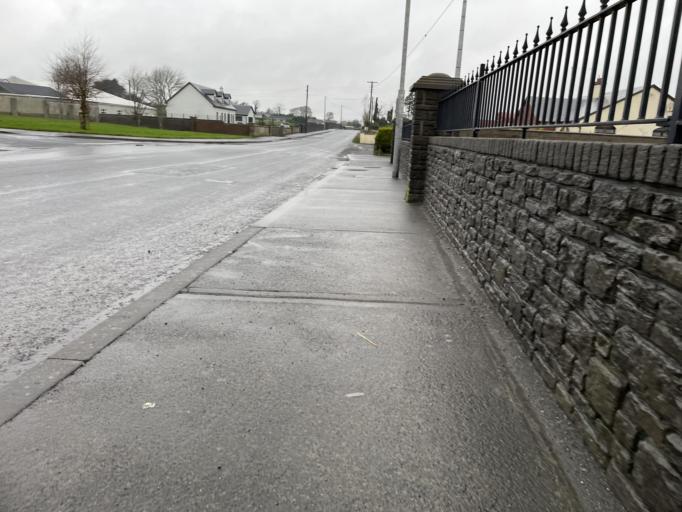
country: IE
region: Connaught
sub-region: County Galway
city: Tuam
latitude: 53.5149
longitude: -8.8655
